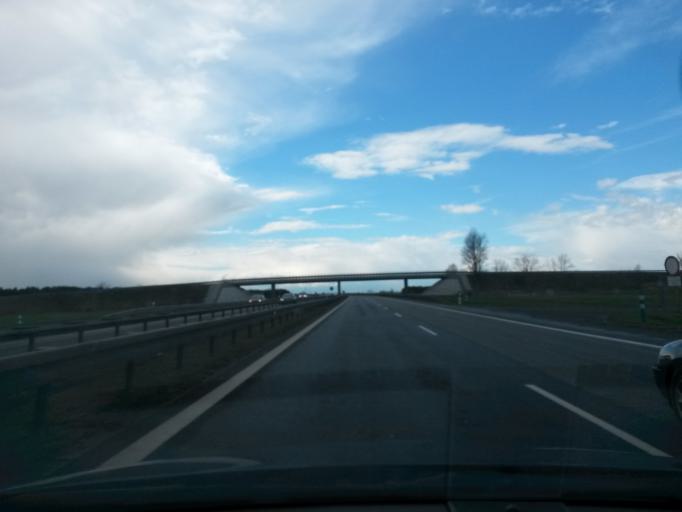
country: PL
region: Greater Poland Voivodeship
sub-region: Powiat slupecki
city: Ladek
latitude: 52.2239
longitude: 17.9439
